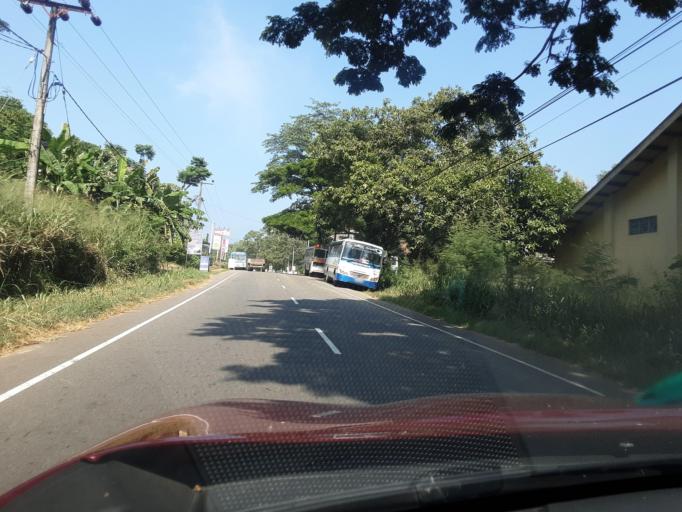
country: LK
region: Uva
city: Badulla
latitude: 7.1852
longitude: 81.0422
